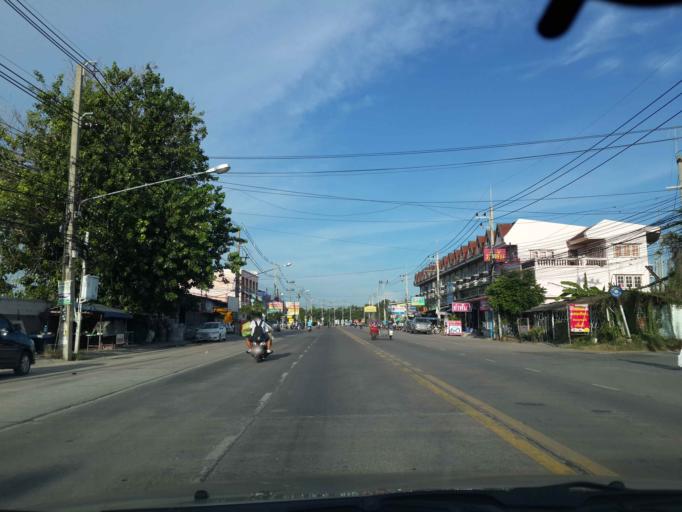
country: TH
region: Chon Buri
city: Phatthaya
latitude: 12.9661
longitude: 100.9152
